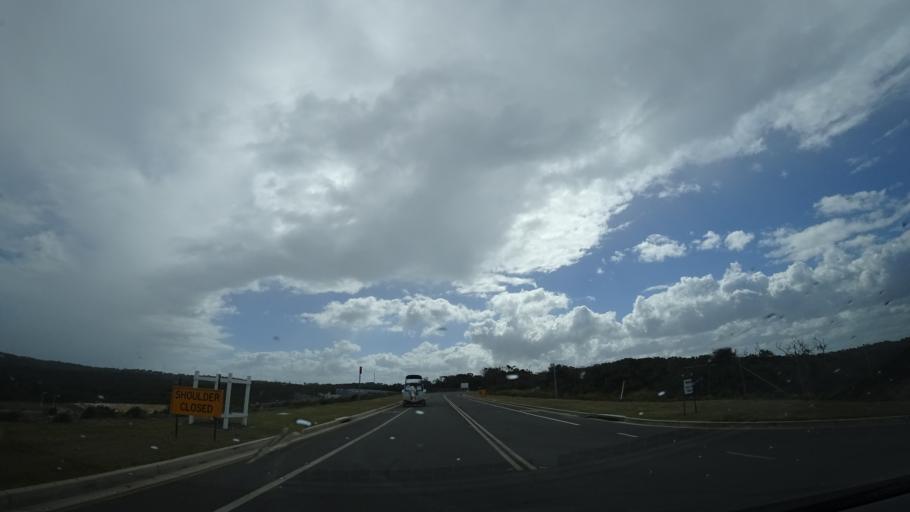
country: AU
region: New South Wales
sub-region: Wyong Shire
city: Kingfisher Shores
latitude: -33.1629
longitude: 151.6218
